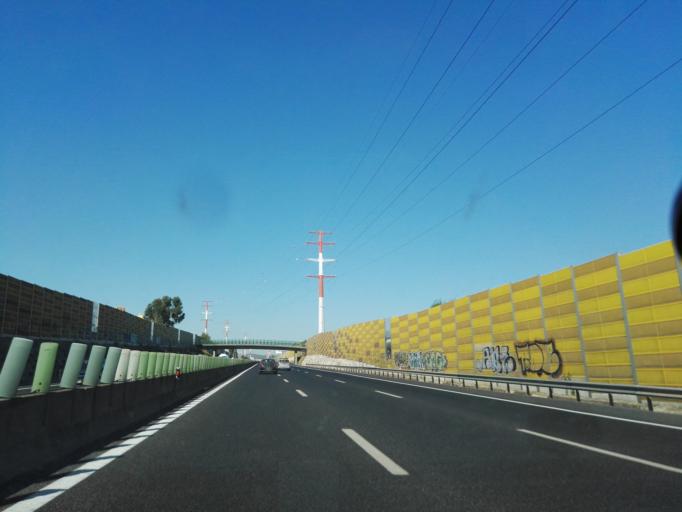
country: PT
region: Lisbon
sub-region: Loures
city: Bobadela
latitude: 38.8168
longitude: -9.1008
